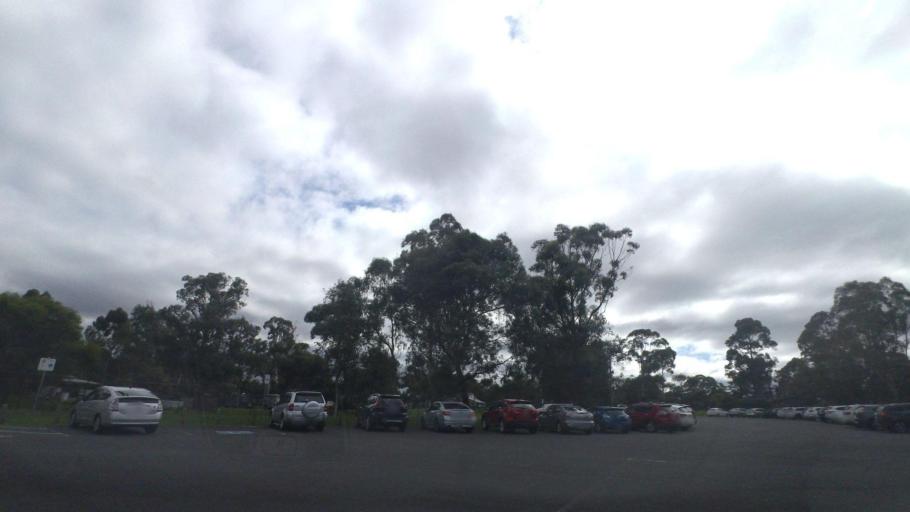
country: AU
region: Victoria
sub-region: Darebin
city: Kingsbury
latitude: -37.7070
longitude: 145.0448
